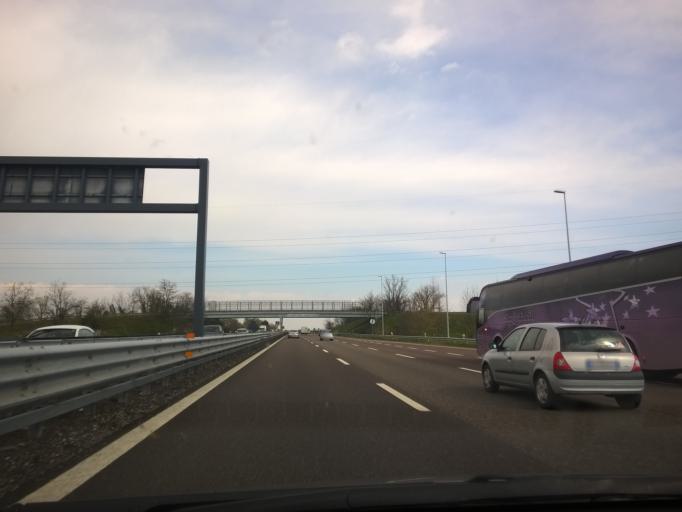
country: IT
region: Lombardy
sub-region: Provincia di Brescia
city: Molinetto
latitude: 45.4805
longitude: 10.3303
